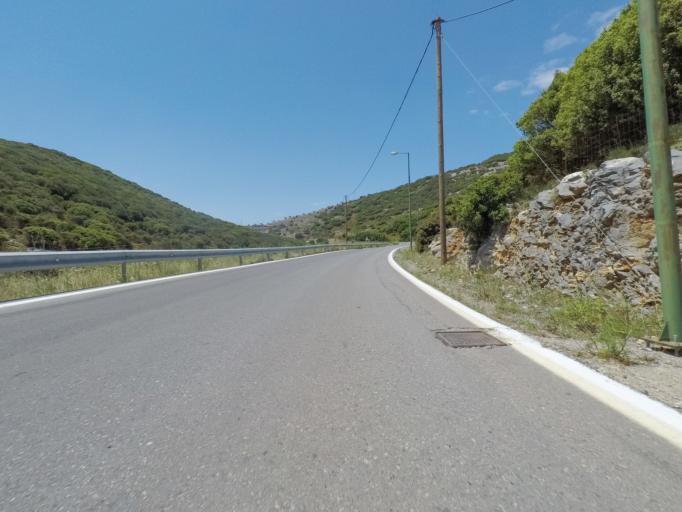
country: GR
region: Crete
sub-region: Nomos Irakleiou
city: Mokhos
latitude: 35.2000
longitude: 25.4602
